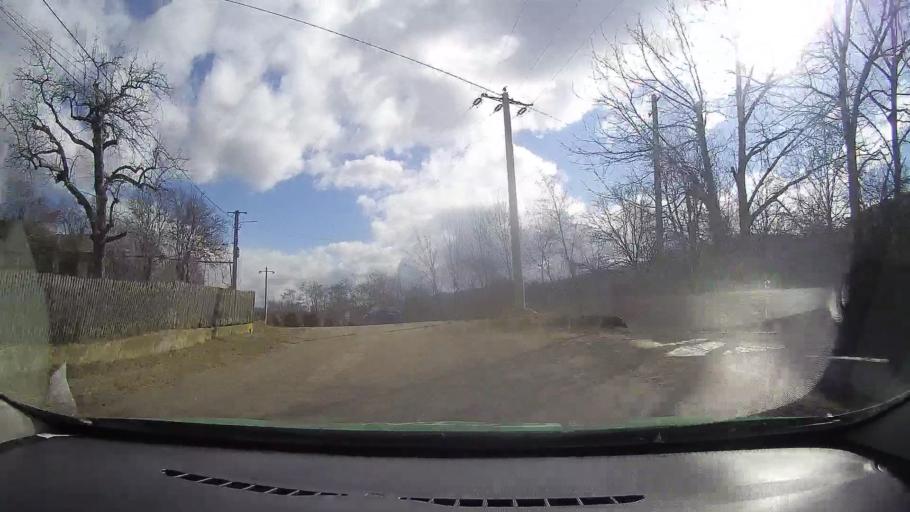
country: RO
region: Dambovita
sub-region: Comuna Buciumeni
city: Buciumeni
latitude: 45.1192
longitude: 25.4511
